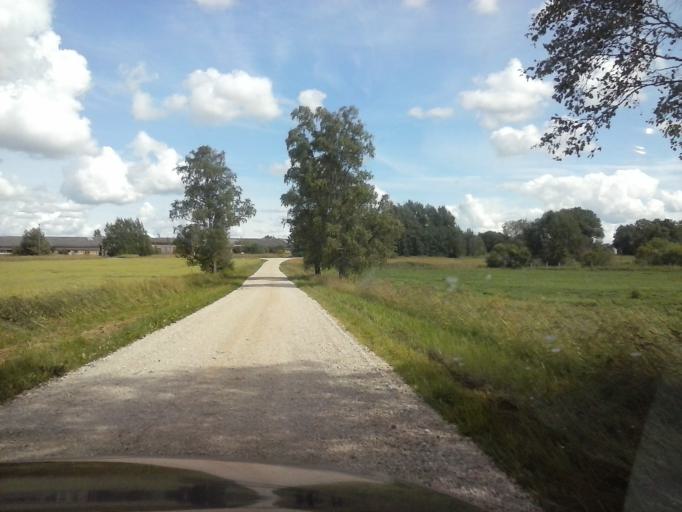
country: EE
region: Laeaene-Virumaa
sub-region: Vaeike-Maarja vald
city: Vaike-Maarja
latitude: 59.0822
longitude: 26.1914
